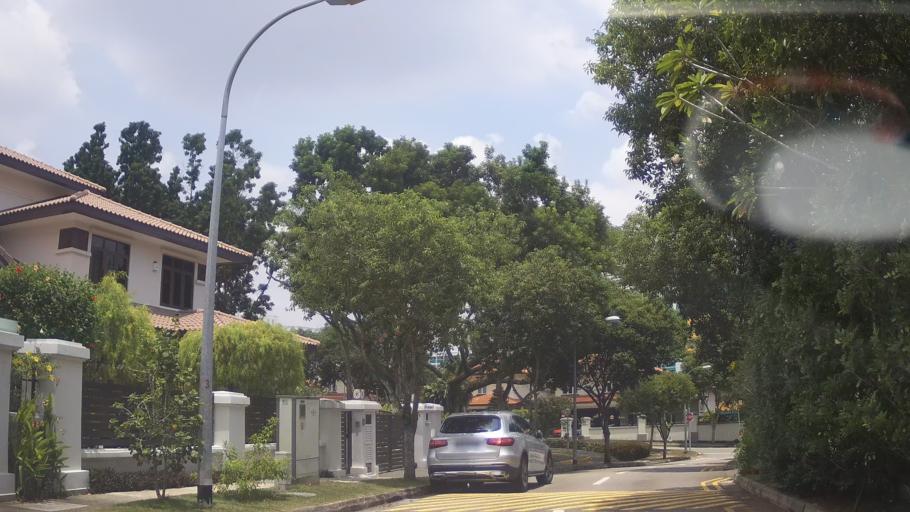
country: MY
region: Johor
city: Johor Bahru
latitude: 1.3728
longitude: 103.7724
